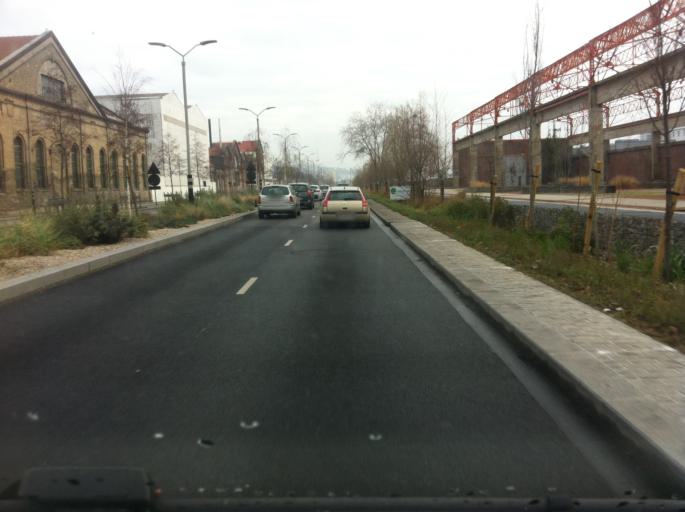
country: FR
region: Haute-Normandie
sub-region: Departement de la Seine-Maritime
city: Le Havre
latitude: 49.4945
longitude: 0.1403
